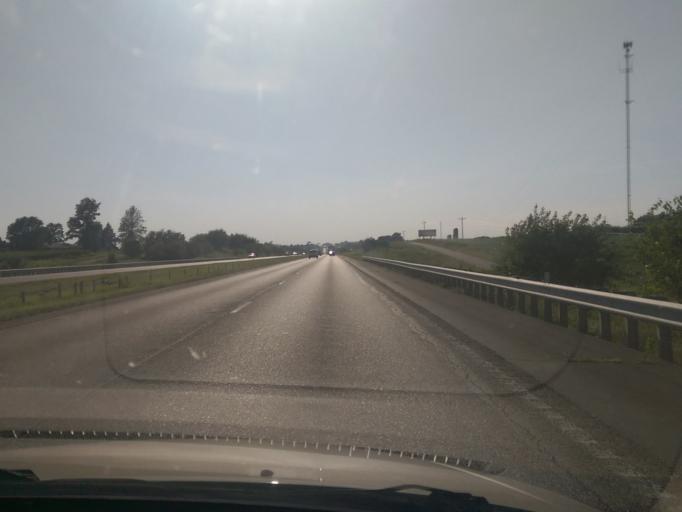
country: US
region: Missouri
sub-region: Lafayette County
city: Odessa
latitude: 39.0062
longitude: -93.8985
